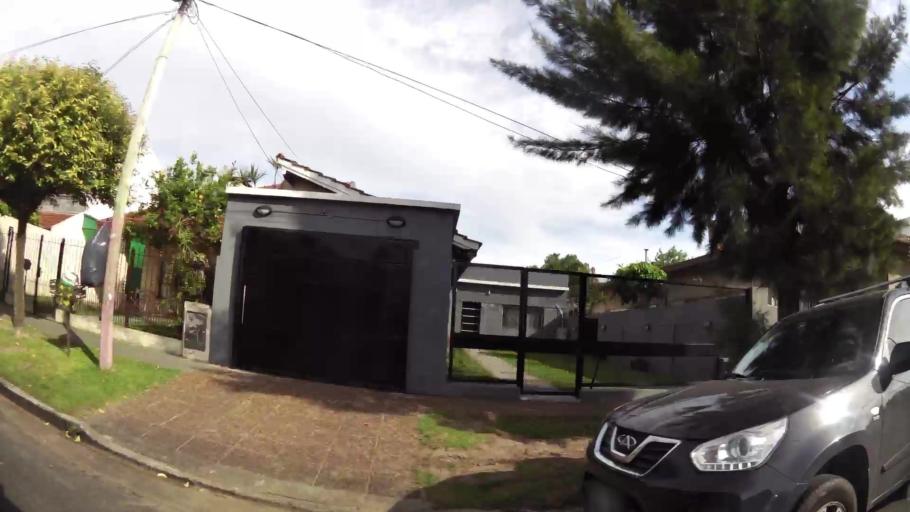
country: AR
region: Buenos Aires
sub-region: Partido de Quilmes
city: Quilmes
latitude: -34.7562
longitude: -58.2869
